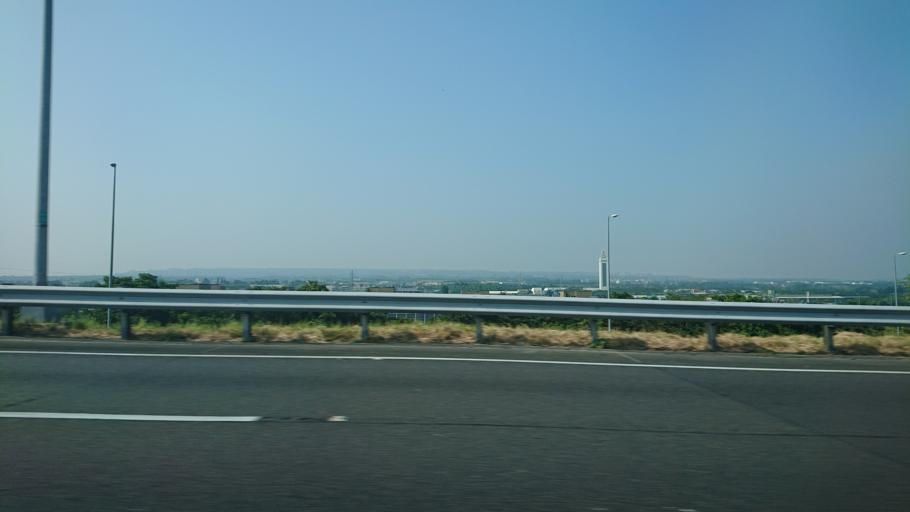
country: TW
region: Taiwan
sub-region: Nantou
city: Nantou
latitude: 23.8504
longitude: 120.7031
